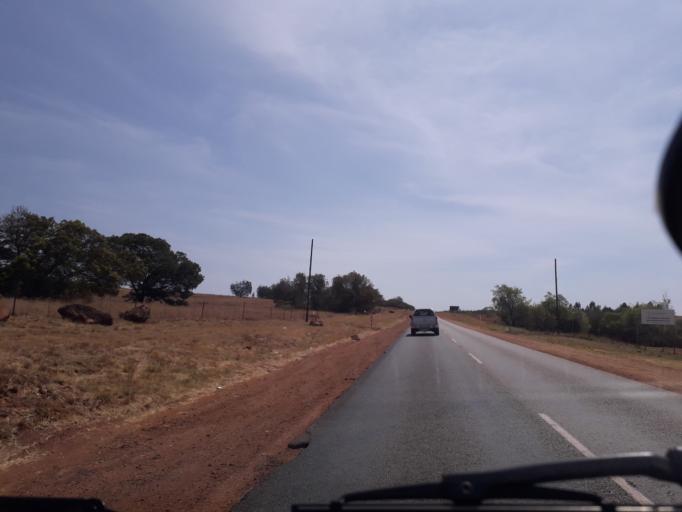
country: ZA
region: Gauteng
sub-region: West Rand District Municipality
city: Krugersdorp
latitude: -25.9968
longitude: 27.7001
